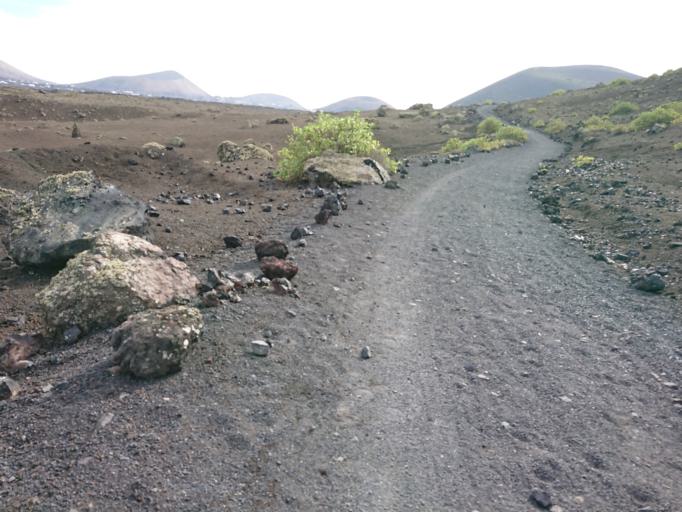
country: ES
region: Canary Islands
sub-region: Provincia de Las Palmas
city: Tias
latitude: 29.0070
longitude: -13.6755
